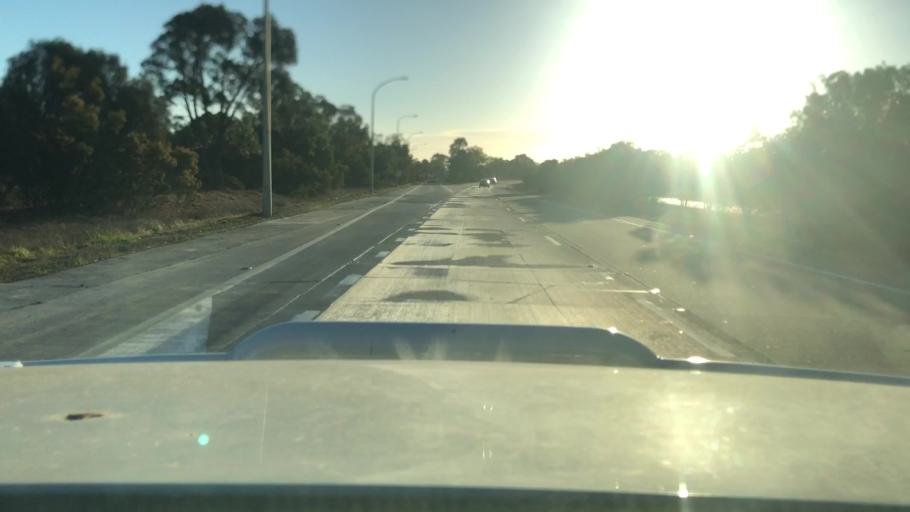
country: AU
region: New South Wales
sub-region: Goulburn Mulwaree
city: Goulburn
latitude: -34.7220
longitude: 149.9928
